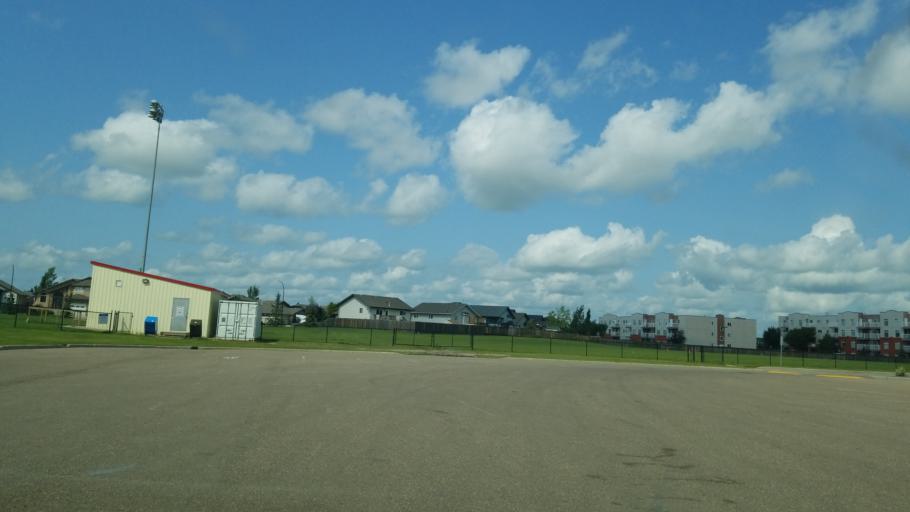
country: CA
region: Saskatchewan
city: Lloydminster
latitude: 53.2510
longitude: -110.0108
